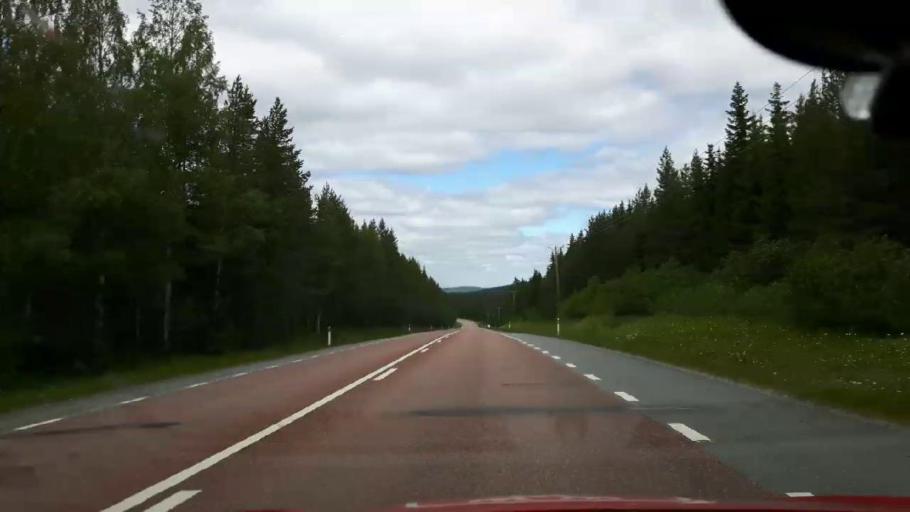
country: SE
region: Jaemtland
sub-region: Braecke Kommun
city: Braecke
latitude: 62.8076
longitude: 15.3677
